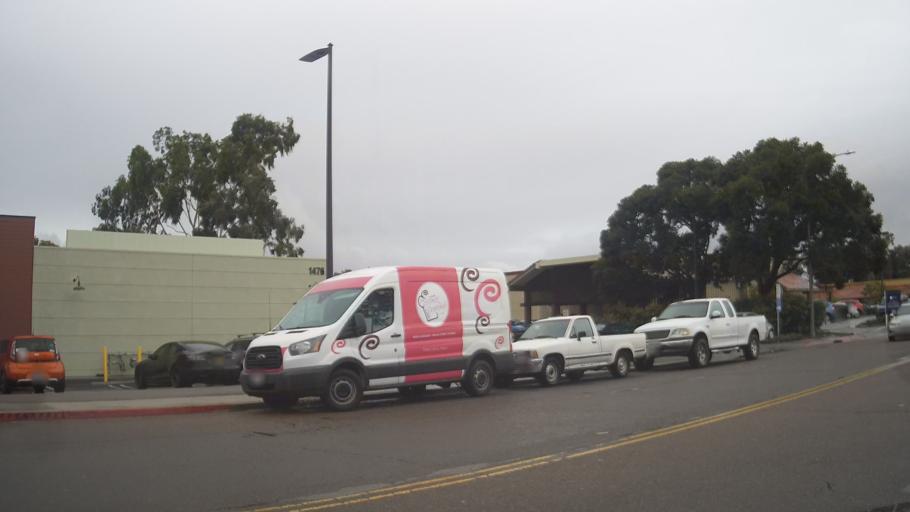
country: US
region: California
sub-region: San Diego County
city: Encinitas
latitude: 33.0466
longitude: -117.2566
